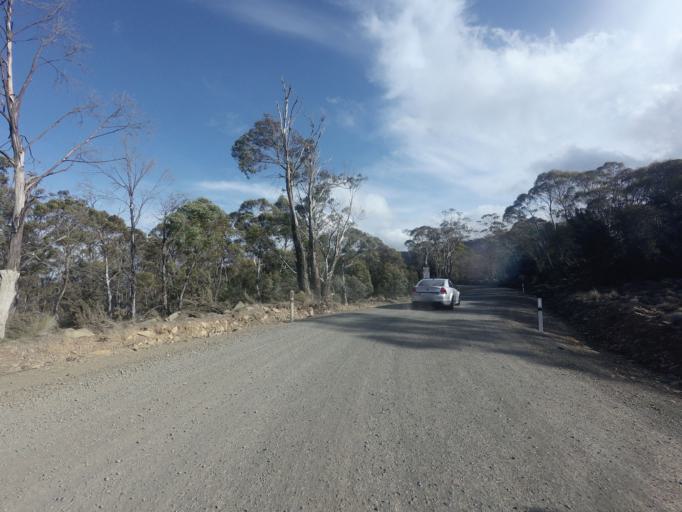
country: AU
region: Tasmania
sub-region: Meander Valley
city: Deloraine
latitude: -41.7776
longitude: 146.7120
